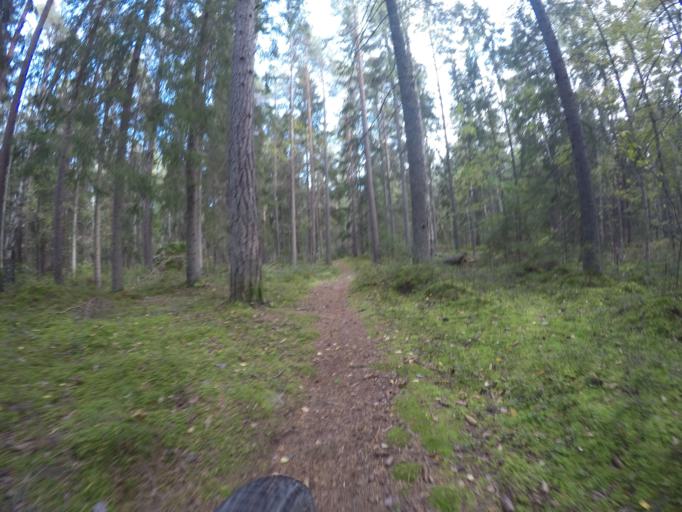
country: SE
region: Vaestmanland
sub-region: Kopings Kommun
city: Koping
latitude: 59.5310
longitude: 16.0003
